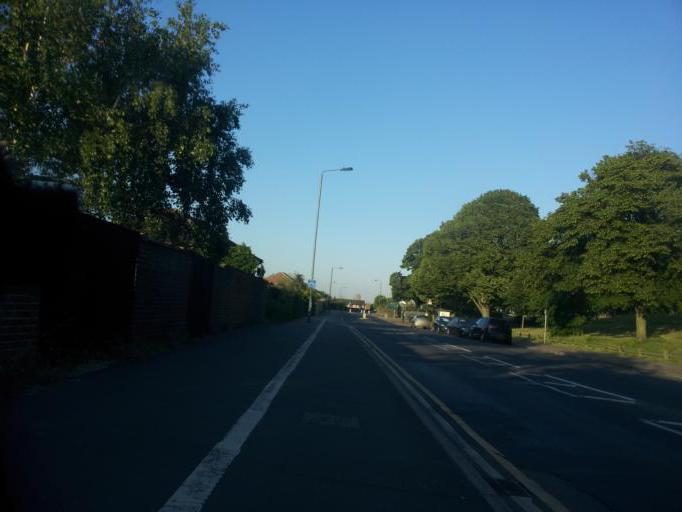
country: GB
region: England
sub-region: Greater London
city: Belvedere
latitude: 51.4903
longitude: 0.1303
